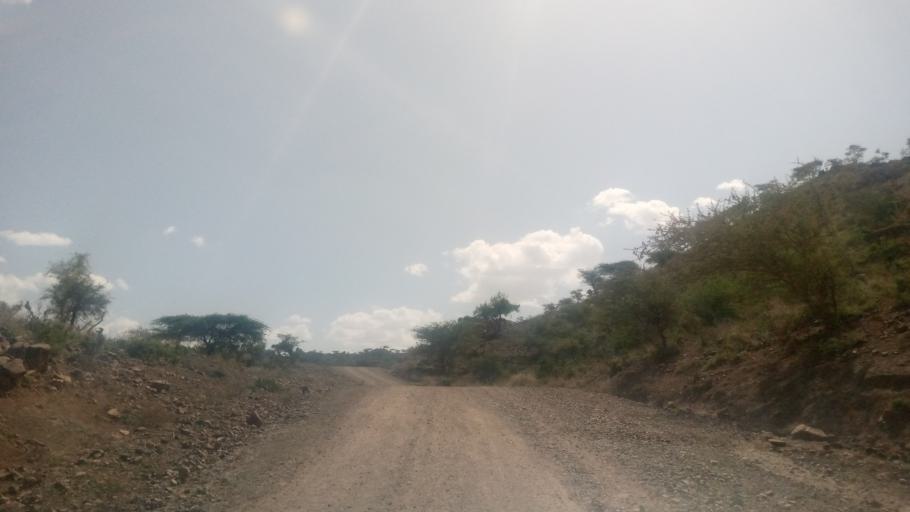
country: ET
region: Oromiya
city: Deder
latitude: 9.5004
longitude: 41.2545
